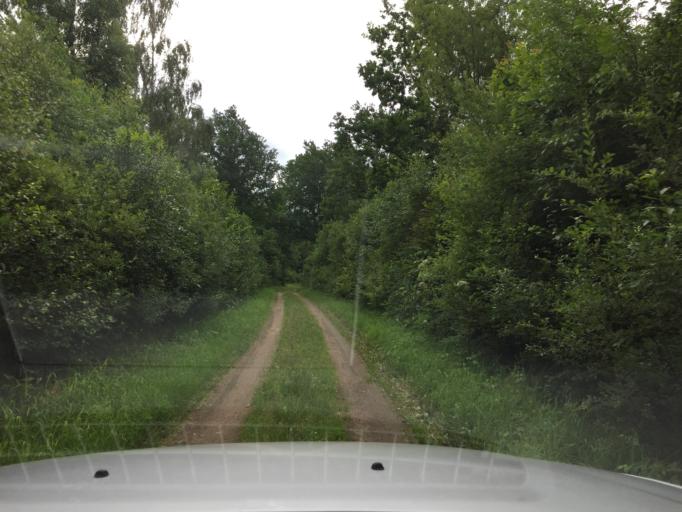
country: SE
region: Skane
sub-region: Hassleholms Kommun
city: Sosdala
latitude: 56.0276
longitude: 13.7000
